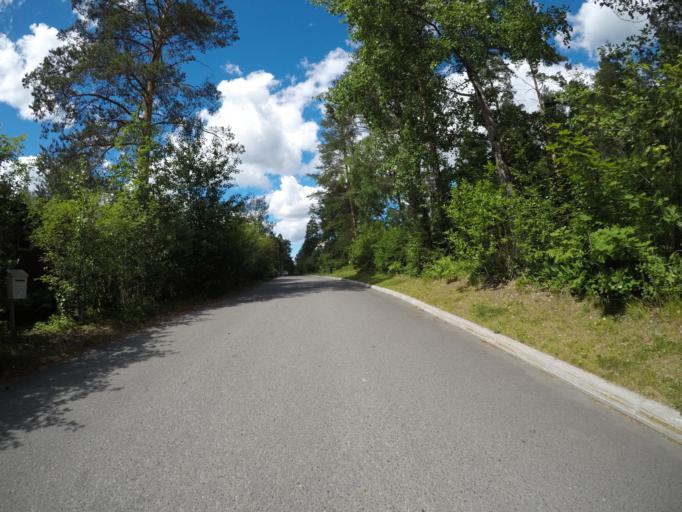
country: FI
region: Haeme
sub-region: Haemeenlinna
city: Haemeenlinna
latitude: 61.0141
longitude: 24.4332
